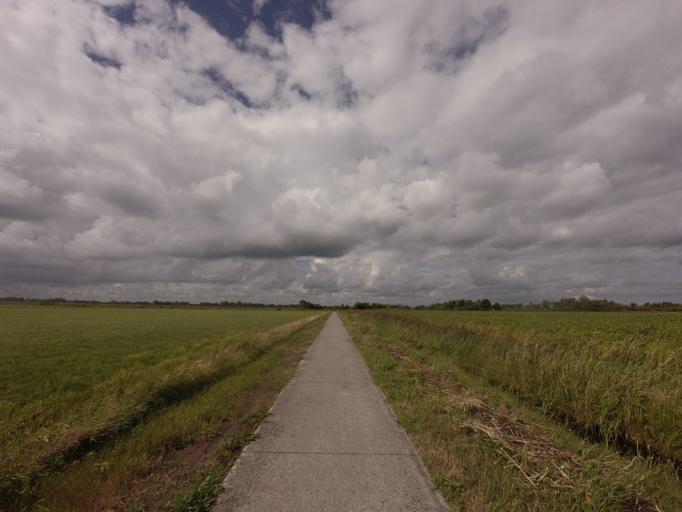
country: NL
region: Overijssel
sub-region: Gemeente Steenwijkerland
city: Wanneperveen
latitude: 52.7083
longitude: 6.1027
